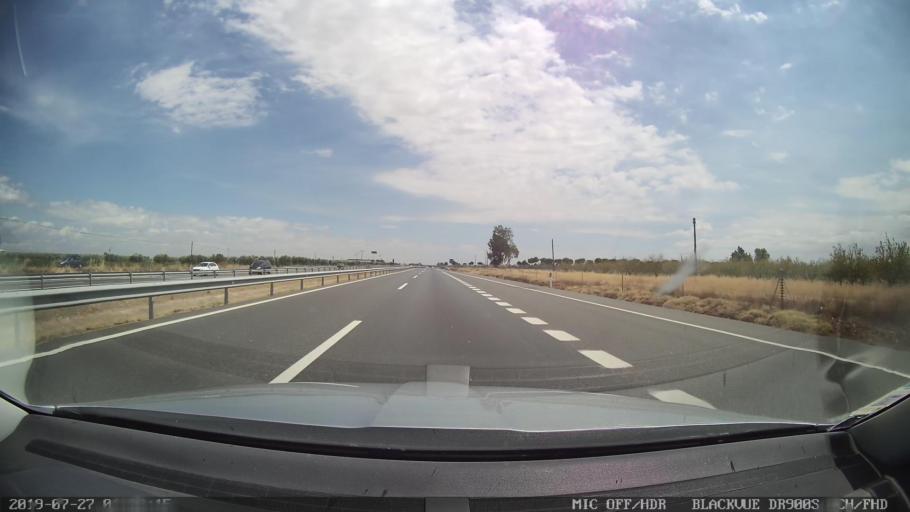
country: ES
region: Castille-La Mancha
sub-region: Province of Toledo
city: Illan de Vacas
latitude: 40.0146
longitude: -4.5687
